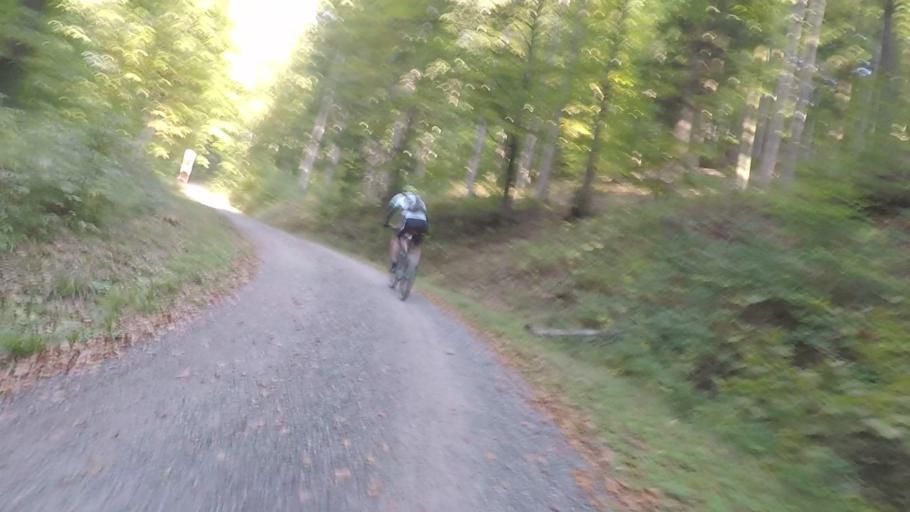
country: DE
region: Baden-Wuerttemberg
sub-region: Regierungsbezirk Stuttgart
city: Spiegelberg
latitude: 49.0439
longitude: 9.4524
